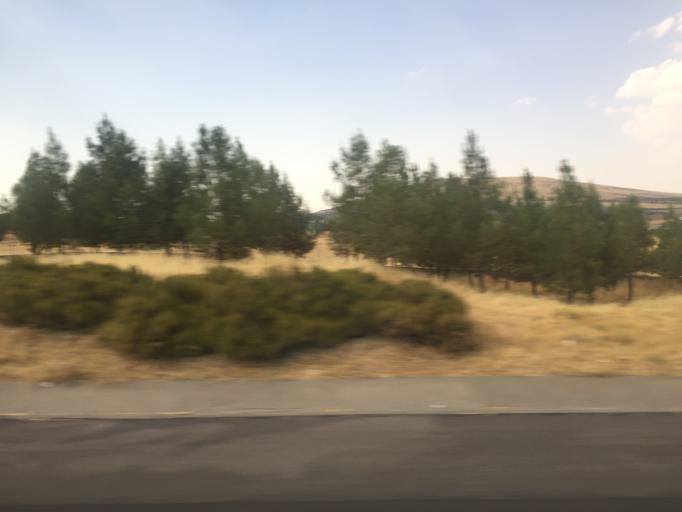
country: TR
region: Sanliurfa
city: Akziyaret
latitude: 37.2626
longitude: 38.7585
